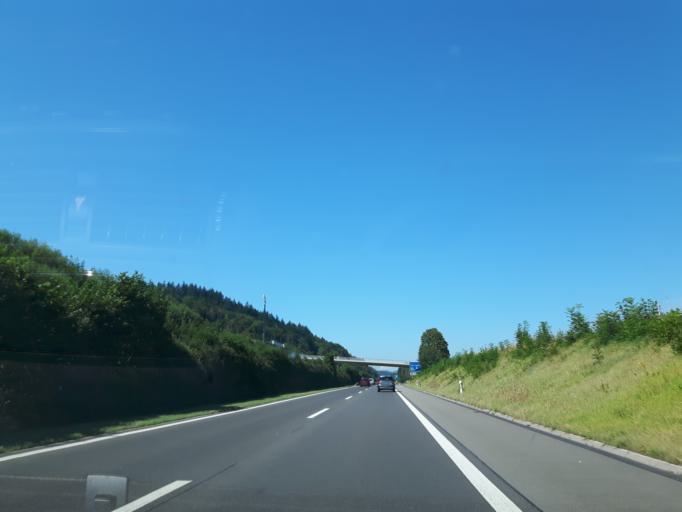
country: CH
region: Zurich
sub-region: Bezirk Horgen
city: Horgen / Allmend
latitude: 47.2358
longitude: 8.6156
